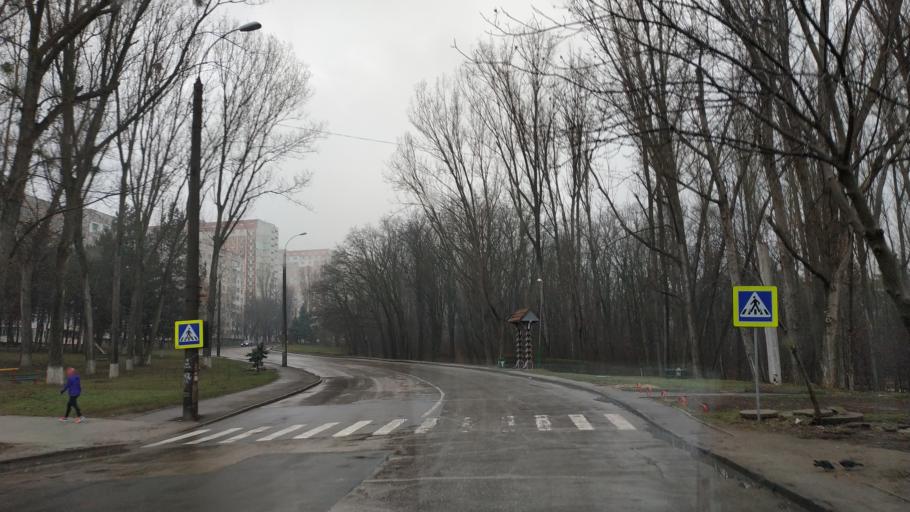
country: MD
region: Chisinau
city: Vatra
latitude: 47.0393
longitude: 28.7799
